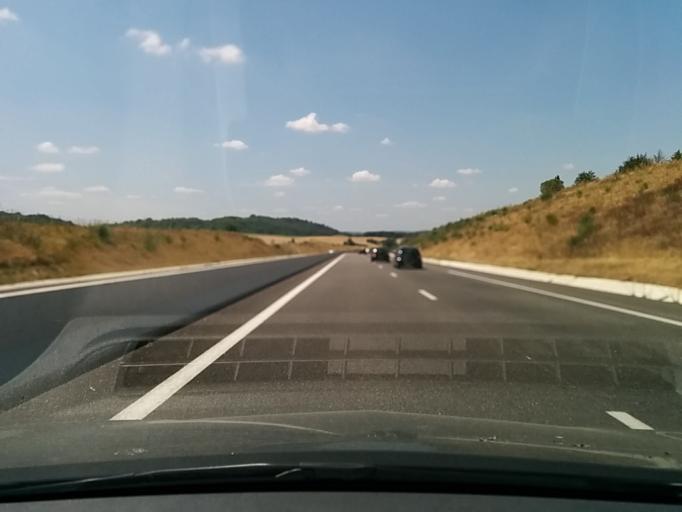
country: FR
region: Midi-Pyrenees
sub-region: Departement du Gers
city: Preignan
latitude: 43.6516
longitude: 0.6744
